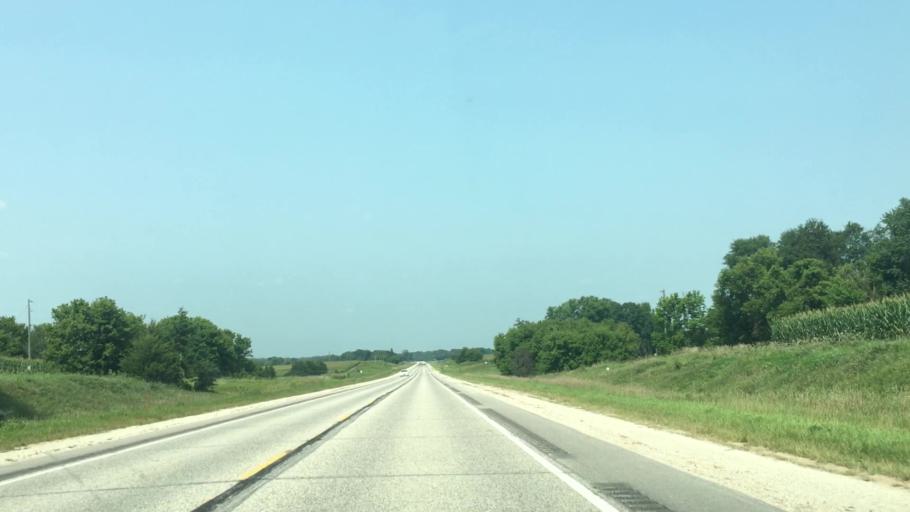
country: US
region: Iowa
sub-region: Fayette County
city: Fayette
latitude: 42.8097
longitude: -91.8052
